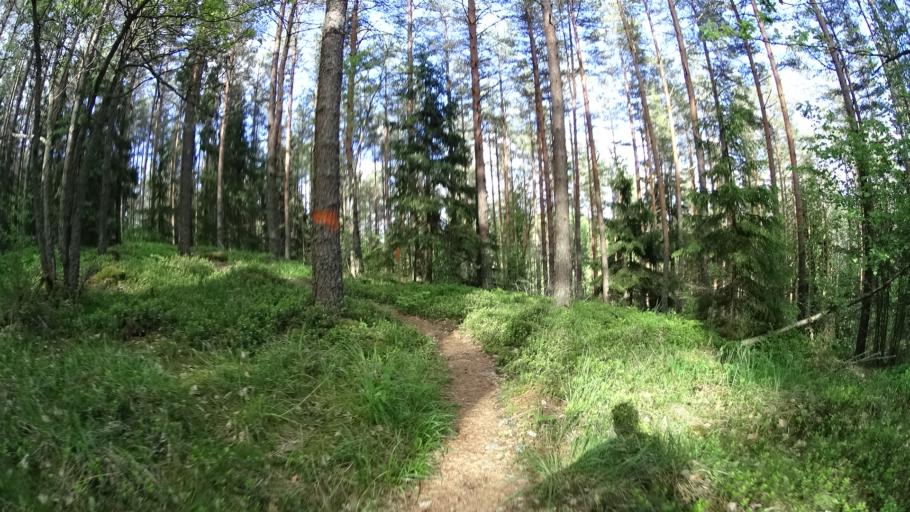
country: FI
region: Uusimaa
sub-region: Raaseporin
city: Pohja
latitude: 60.1398
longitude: 23.5333
